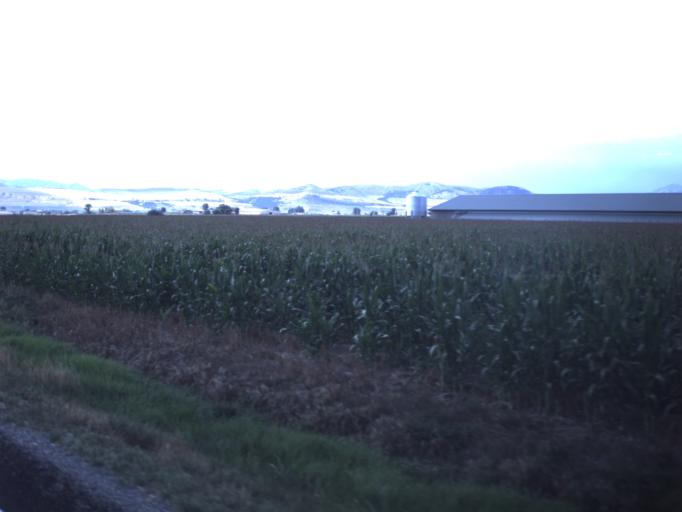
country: US
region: Utah
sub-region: Cache County
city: Lewiston
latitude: 41.9247
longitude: -111.9009
